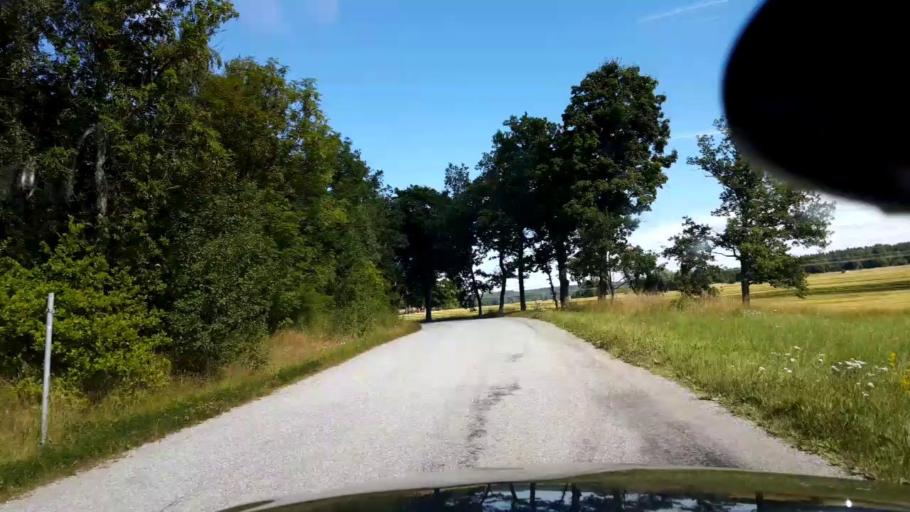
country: SE
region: Stockholm
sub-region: Upplands-Bro Kommun
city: Bro
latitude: 59.5942
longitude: 17.6416
